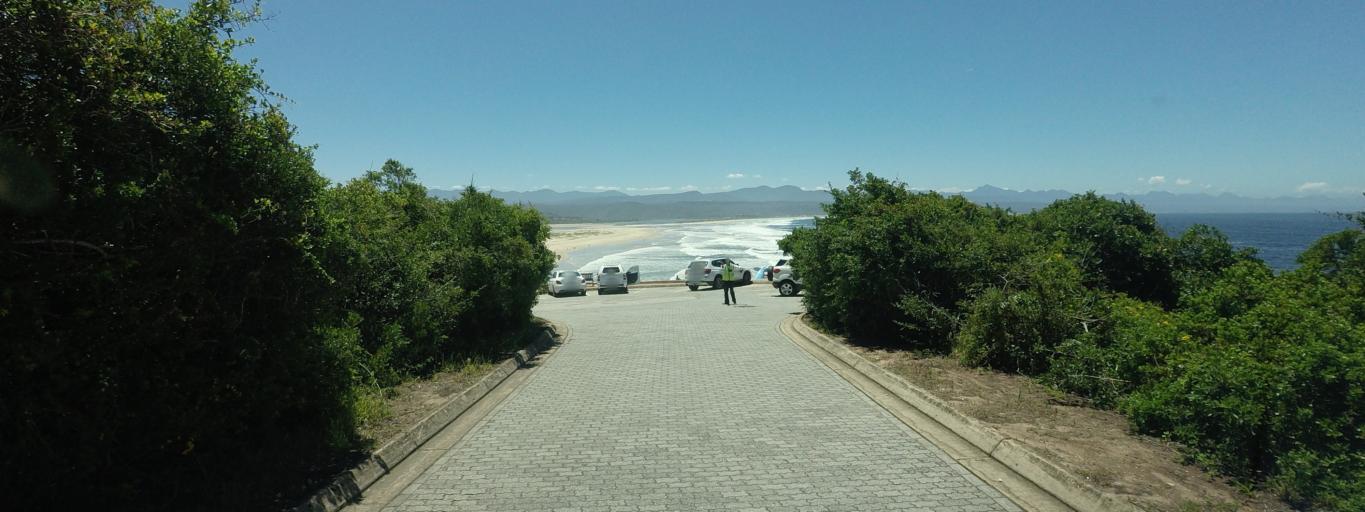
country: ZA
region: Western Cape
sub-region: Eden District Municipality
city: Plettenberg Bay
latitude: -34.0531
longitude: 23.3777
